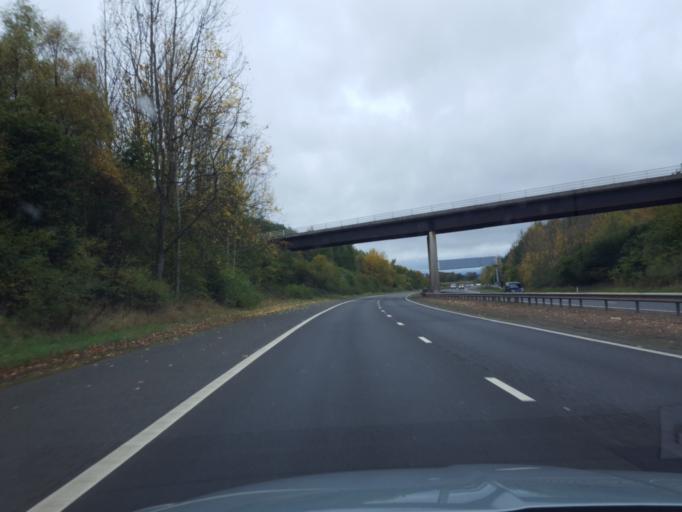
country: GB
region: Scotland
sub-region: Edinburgh
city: Balerno
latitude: 55.9206
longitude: -3.3405
